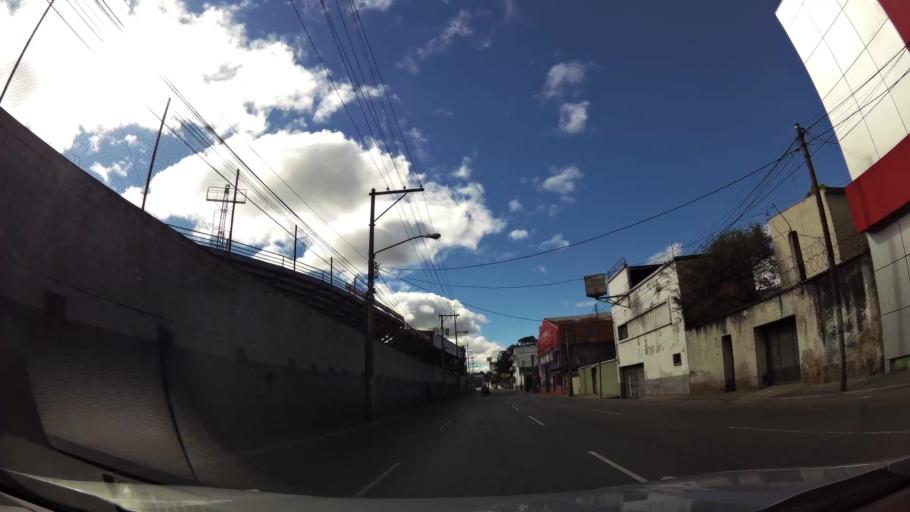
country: GT
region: Guatemala
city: Guatemala City
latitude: 14.6165
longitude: -90.5103
